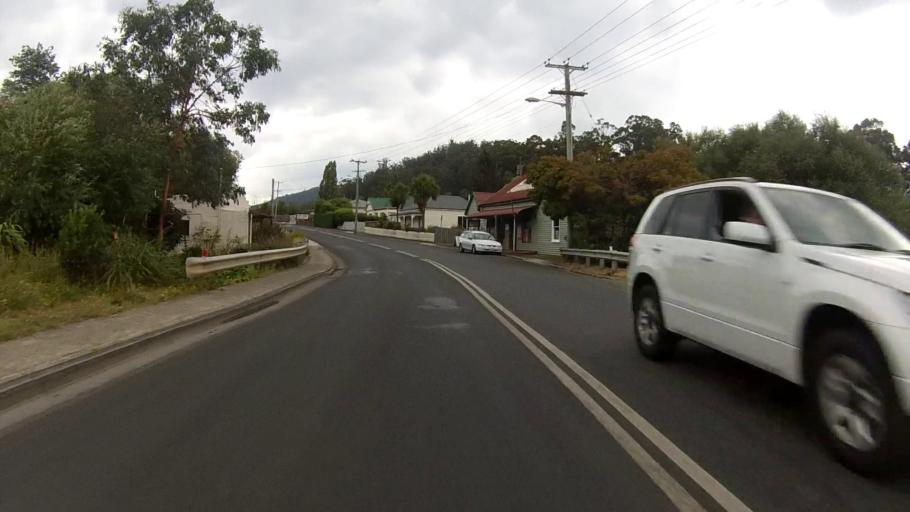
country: AU
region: Tasmania
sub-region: Huon Valley
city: Cygnet
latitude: -43.1552
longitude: 147.0739
